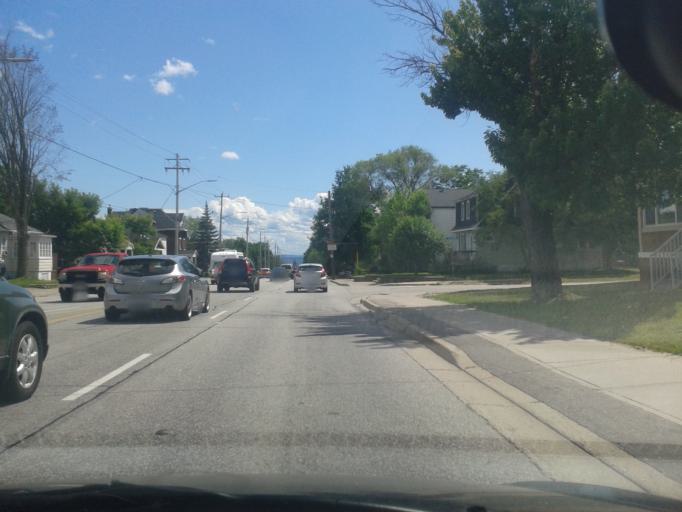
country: CA
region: Ontario
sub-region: Nipissing District
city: North Bay
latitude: 46.3252
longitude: -79.4663
